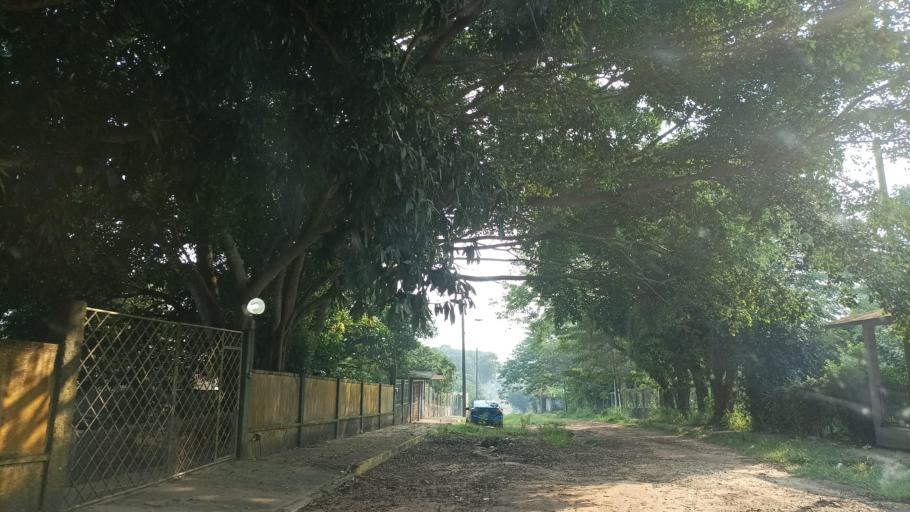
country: MX
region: Veracruz
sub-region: Cosoleacaque
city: Residencial las Olas
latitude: 18.0986
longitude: -94.5705
